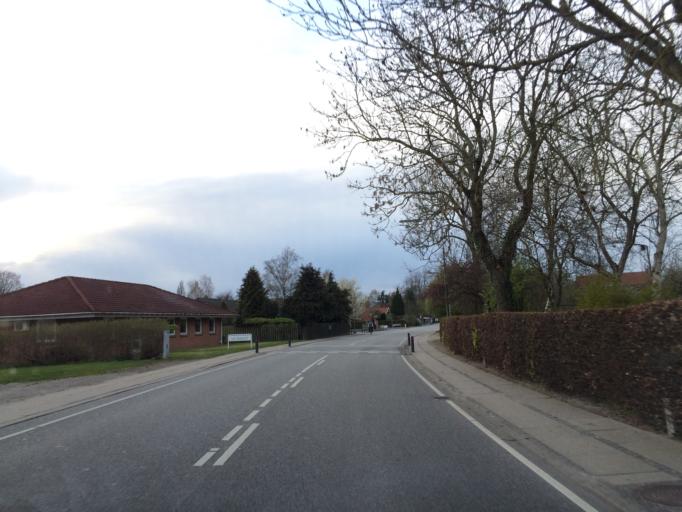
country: DK
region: South Denmark
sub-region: Odense Kommune
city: Bellinge
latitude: 55.3341
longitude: 10.3185
